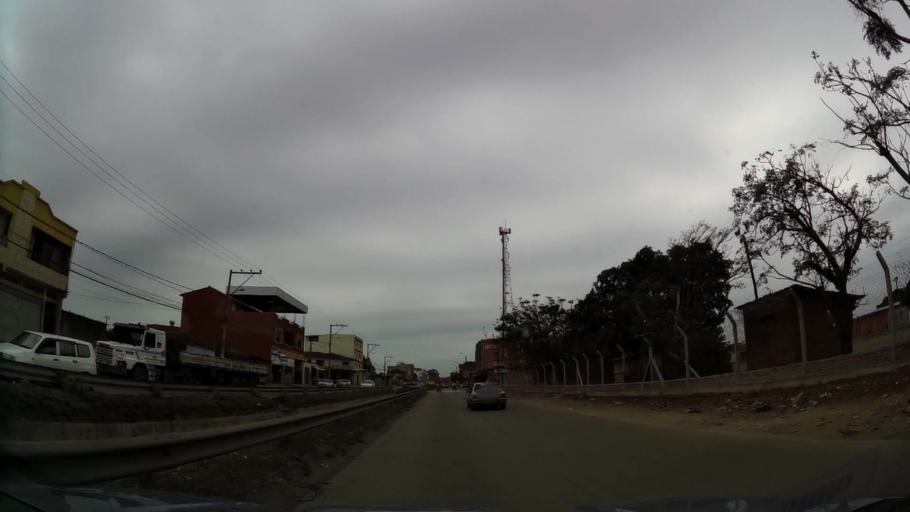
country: BO
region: Santa Cruz
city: Santa Cruz de la Sierra
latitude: -17.8272
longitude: -63.1699
